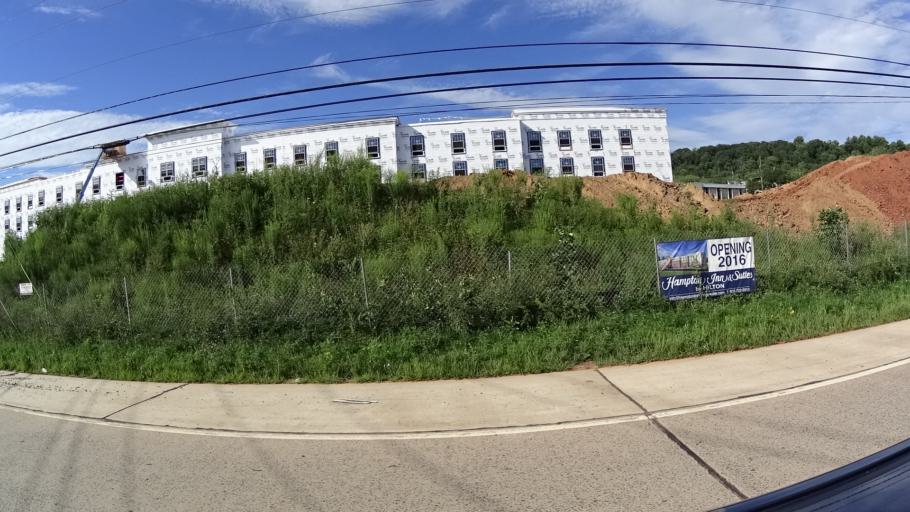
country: US
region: New Jersey
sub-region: Somerset County
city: Finderne
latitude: 40.5776
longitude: -74.5784
